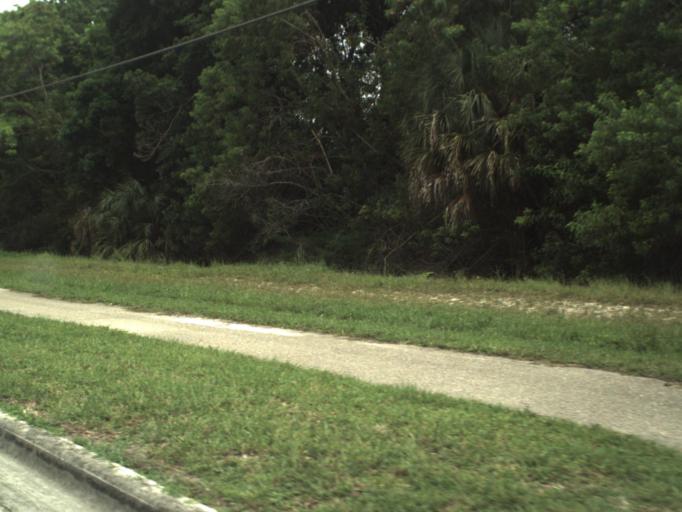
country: US
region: Florida
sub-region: Palm Beach County
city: Boca Pointe
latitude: 26.3493
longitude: -80.1798
